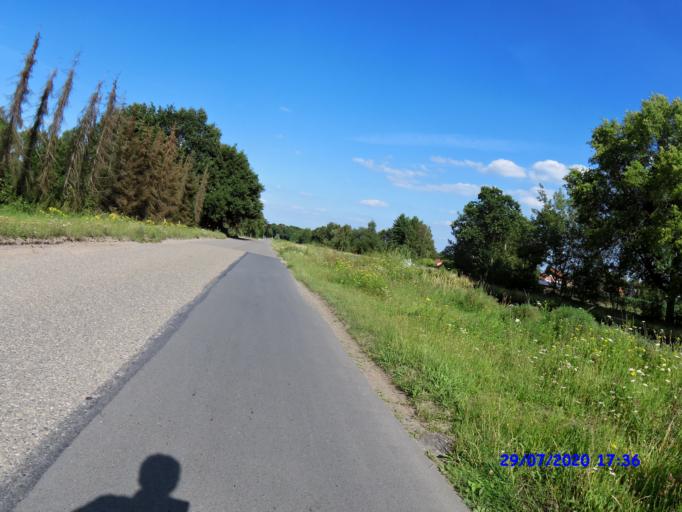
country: BE
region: Flanders
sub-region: Provincie Antwerpen
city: Beerse
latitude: 51.3299
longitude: 4.8736
